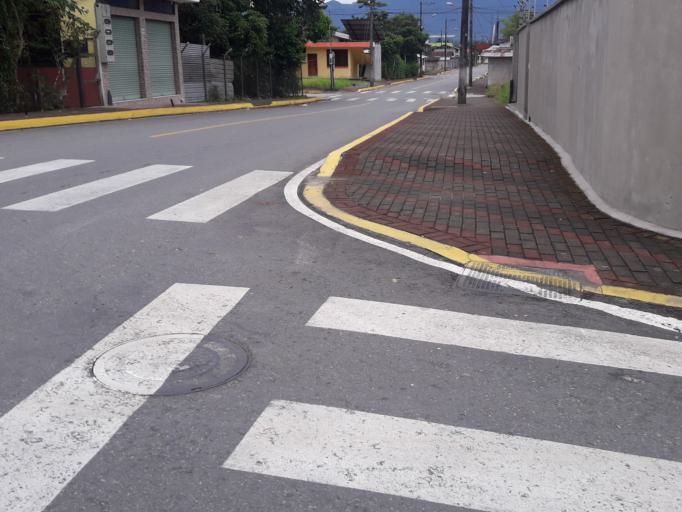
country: EC
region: Napo
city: Tena
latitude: -1.0061
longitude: -77.8133
